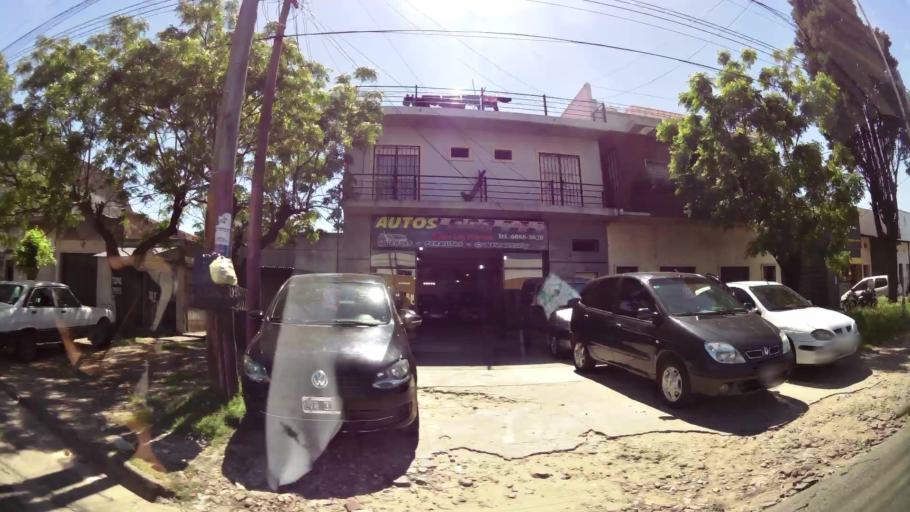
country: AR
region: Buenos Aires
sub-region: Partido de Quilmes
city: Quilmes
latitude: -34.7142
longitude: -58.3069
